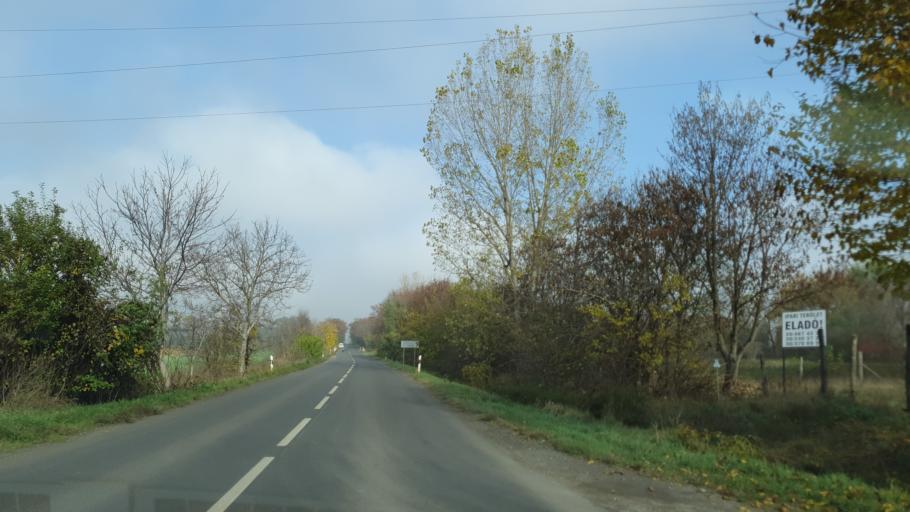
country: HU
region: Pest
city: Orbottyan
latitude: 47.6613
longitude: 19.2376
